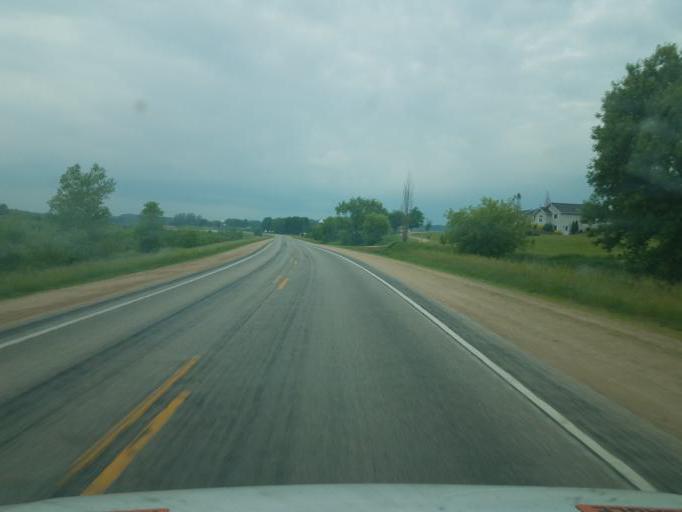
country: US
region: Wisconsin
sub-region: Vernon County
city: Hillsboro
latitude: 43.6582
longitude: -90.3691
